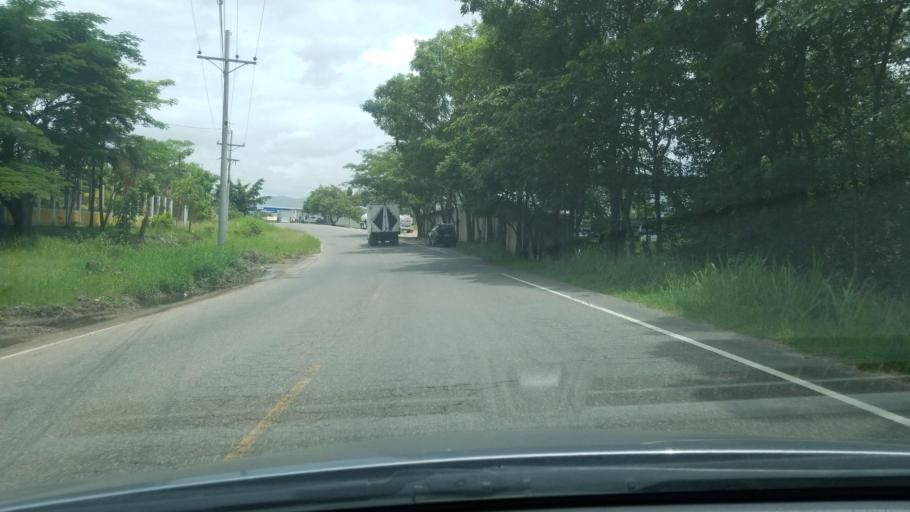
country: HN
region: Copan
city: Cucuyagua
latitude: 14.6688
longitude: -88.8647
